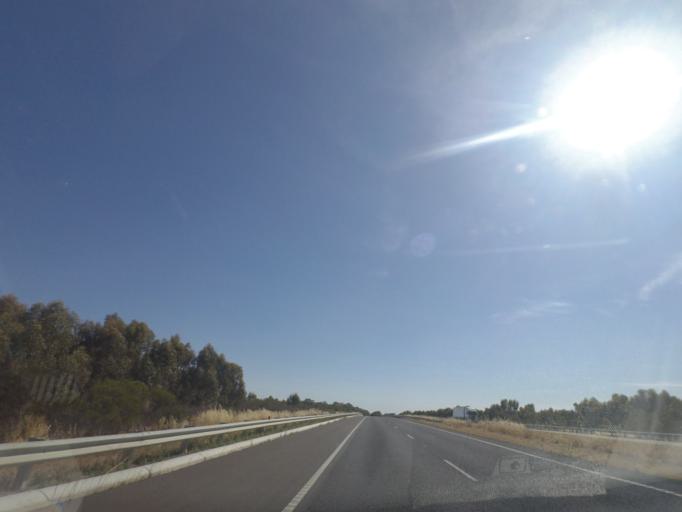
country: AU
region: Victoria
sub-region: Greater Shepparton
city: Shepparton
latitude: -36.6787
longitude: 145.2417
